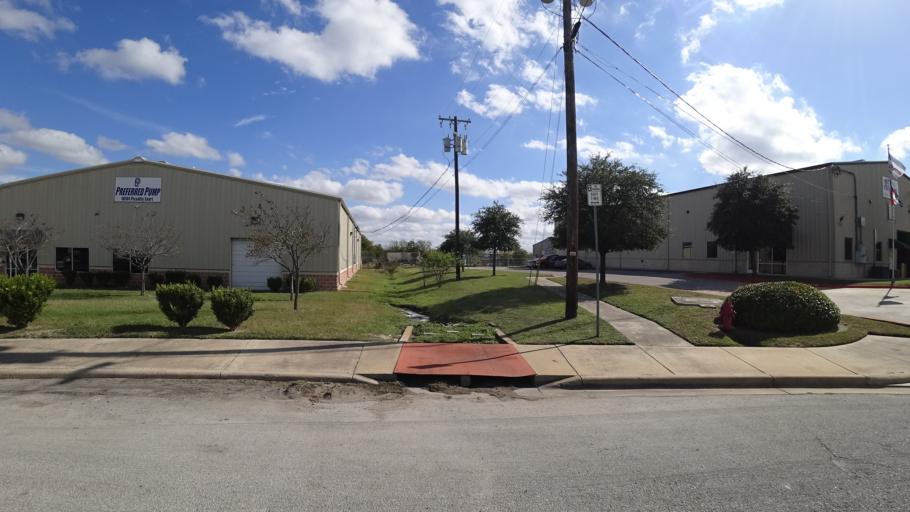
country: US
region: Texas
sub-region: Travis County
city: Windemere
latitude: 30.4659
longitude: -97.6580
